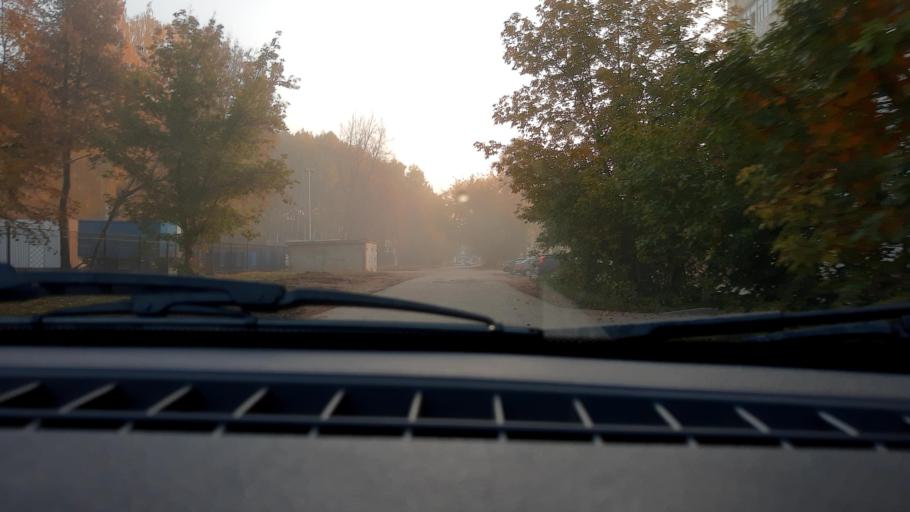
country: RU
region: Bashkortostan
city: Mikhaylovka
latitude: 54.7877
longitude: 55.8772
